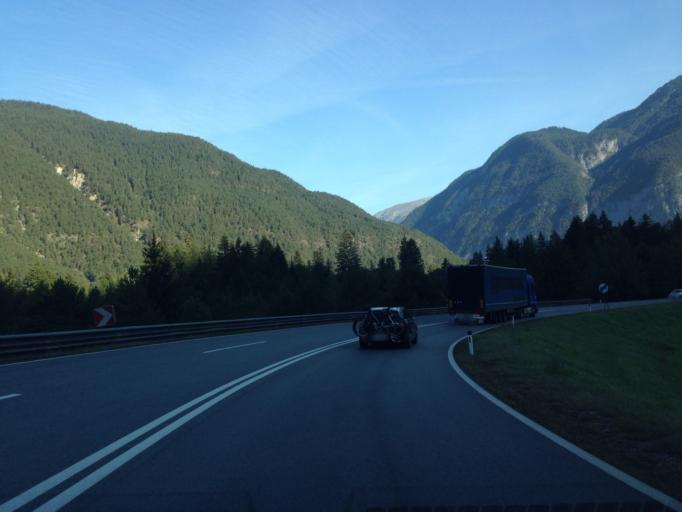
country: AT
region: Tyrol
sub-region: Politischer Bezirk Imst
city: Nassereith
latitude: 47.2925
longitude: 10.8409
